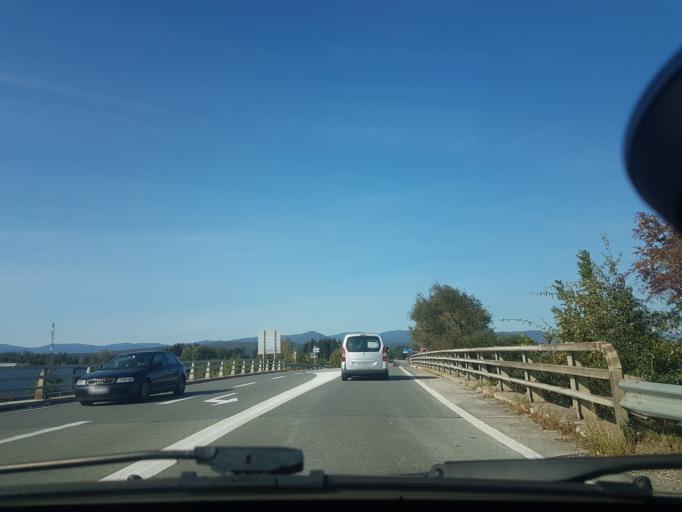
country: FR
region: Franche-Comte
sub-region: Territoire de Belfort
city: Chevremont
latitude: 47.6430
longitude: 6.9172
